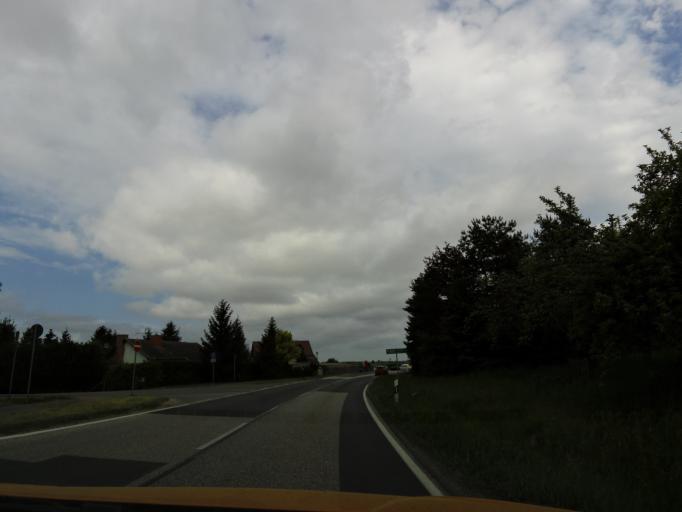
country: DE
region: Brandenburg
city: Niemegk
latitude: 52.0812
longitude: 12.6970
